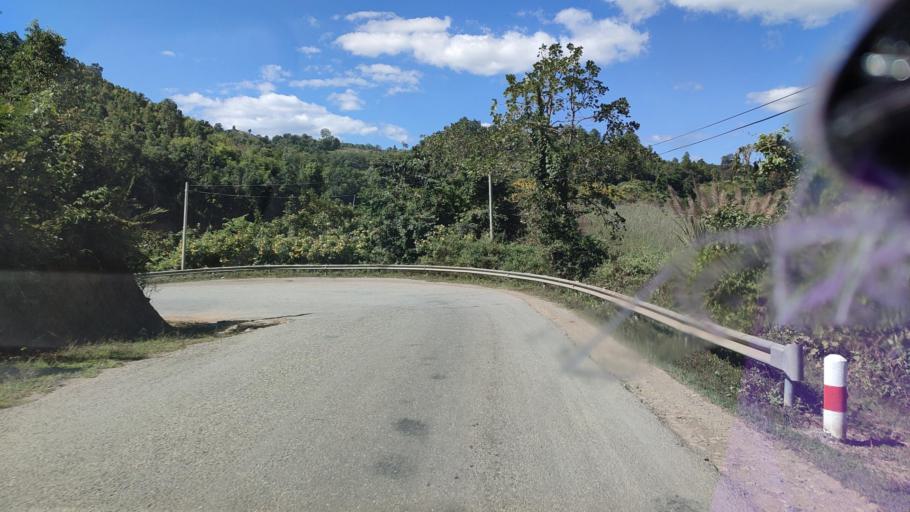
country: MM
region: Shan
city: Taunggyi
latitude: 20.8183
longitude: 97.3903
